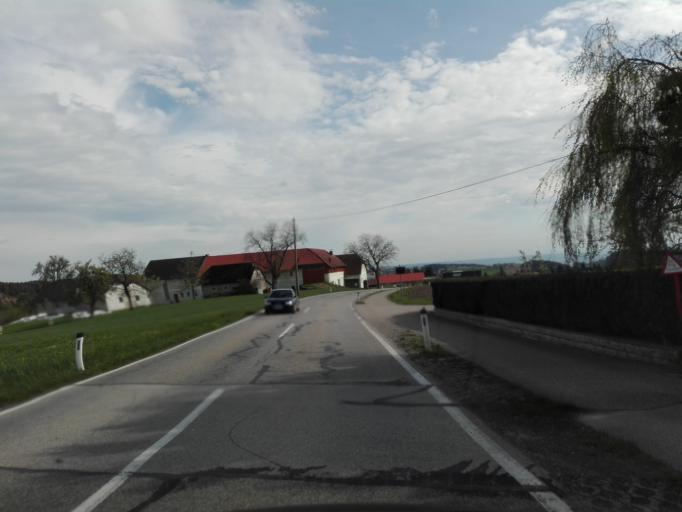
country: AT
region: Upper Austria
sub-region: Politischer Bezirk Rohrbach
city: Kleinzell im Muehlkreis
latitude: 48.4315
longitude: 14.0324
